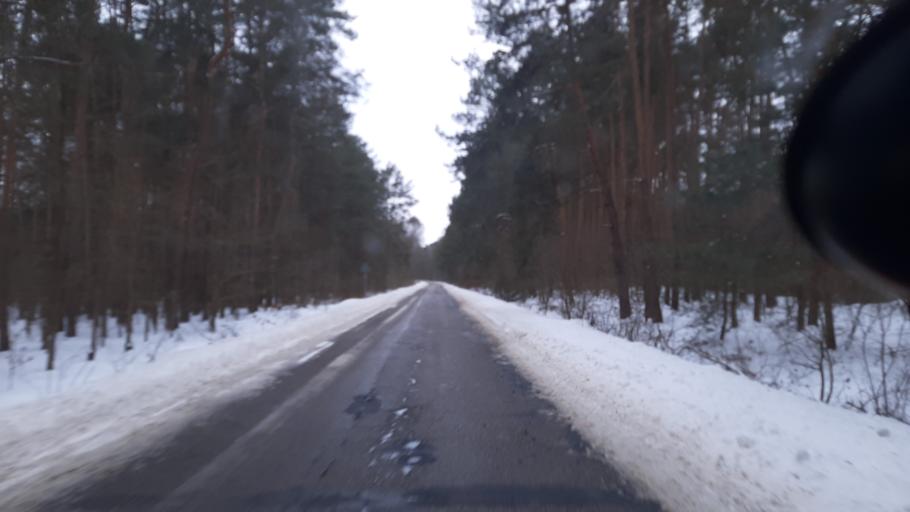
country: PL
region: Lublin Voivodeship
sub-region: Powiat pulawski
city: Markuszow
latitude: 51.4367
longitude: 22.2521
